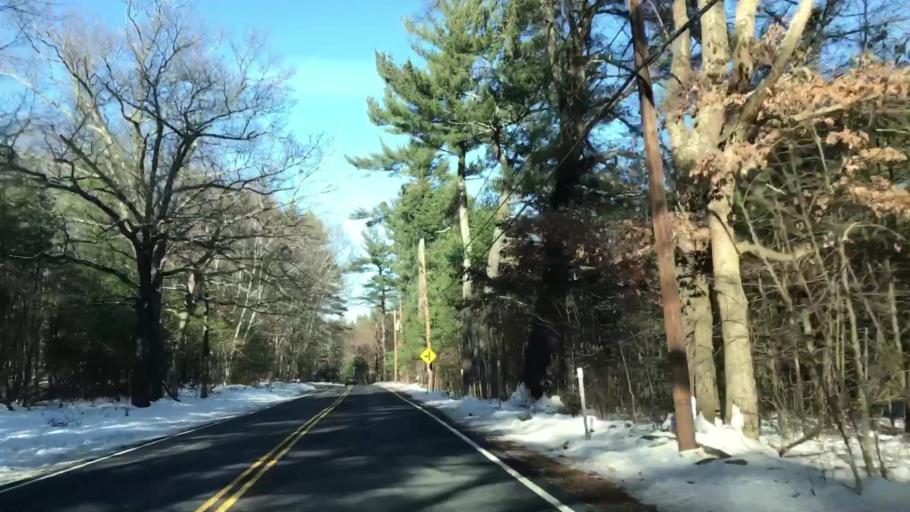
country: US
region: New Hampshire
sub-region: Hillsborough County
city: Milford
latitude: 42.8382
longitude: -71.6132
